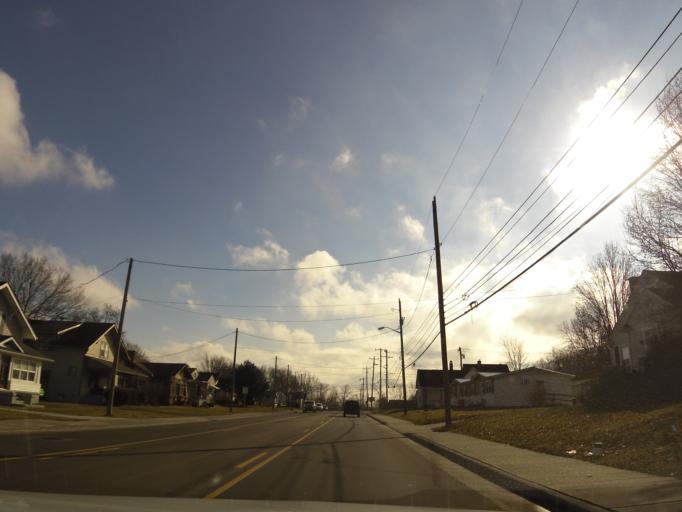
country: US
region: Indiana
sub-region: Jennings County
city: North Vernon
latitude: 38.9982
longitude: -85.6203
